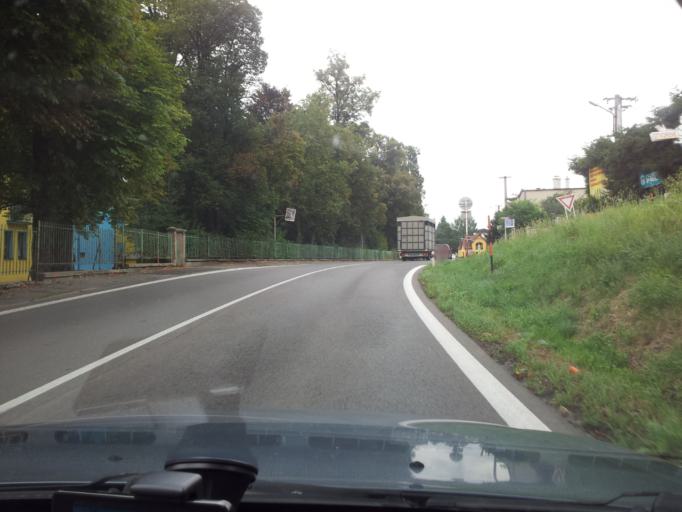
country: SK
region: Presovsky
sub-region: Okres Presov
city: Kezmarok
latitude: 49.1312
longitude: 20.4207
